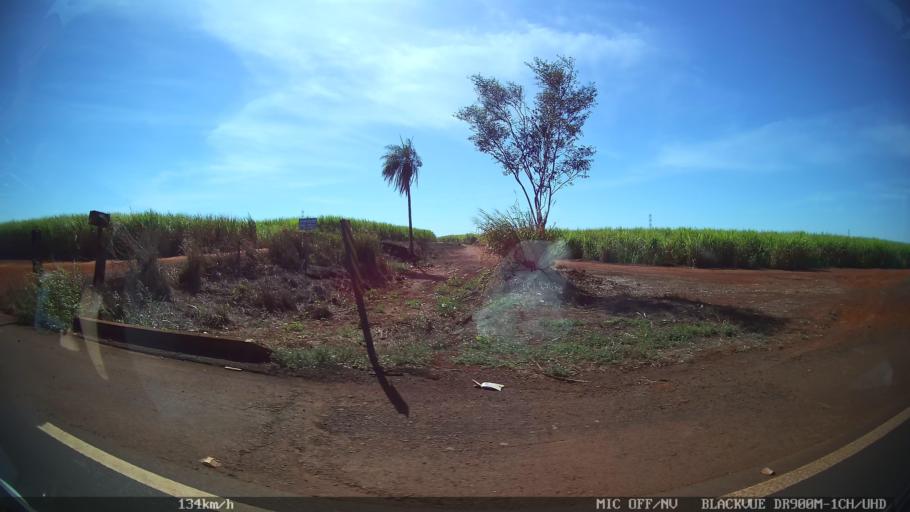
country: BR
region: Sao Paulo
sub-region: Guaira
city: Guaira
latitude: -20.4438
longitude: -48.3057
